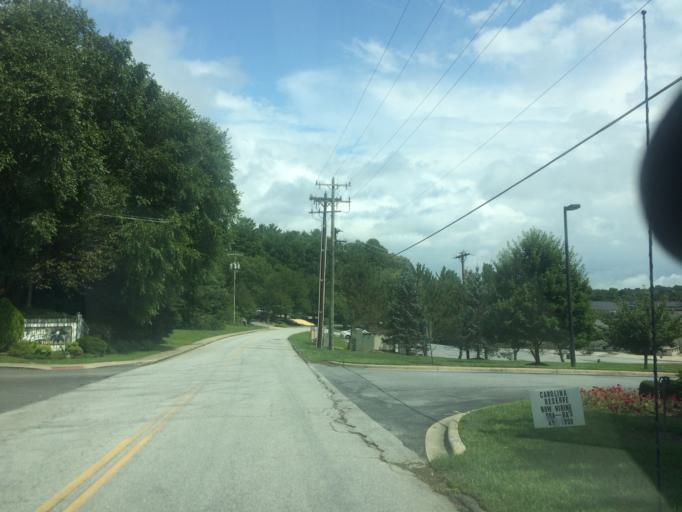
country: US
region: North Carolina
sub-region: Henderson County
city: Laurel Park
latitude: 35.3236
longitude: -82.4920
